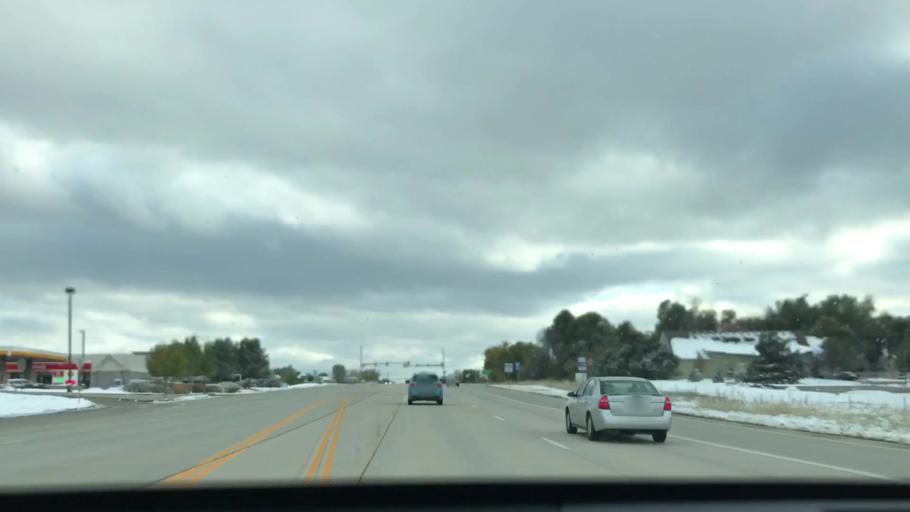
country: US
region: Colorado
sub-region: Boulder County
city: Lafayette
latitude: 40.0176
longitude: -105.1030
